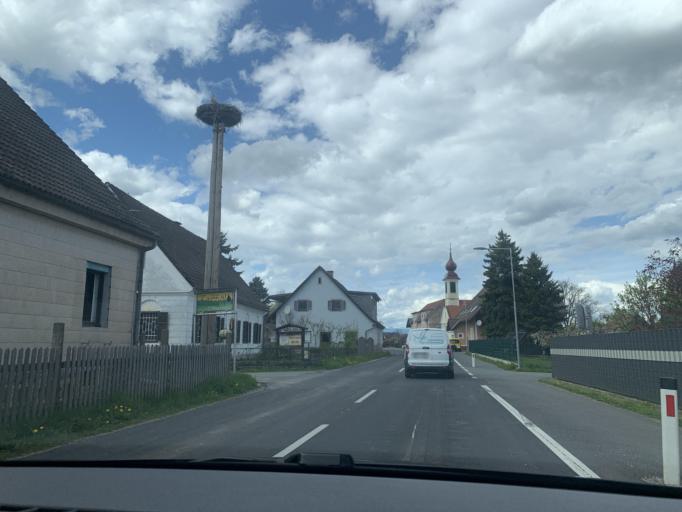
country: AT
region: Styria
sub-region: Politischer Bezirk Graz-Umgebung
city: Zettling
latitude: 46.9192
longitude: 15.4018
